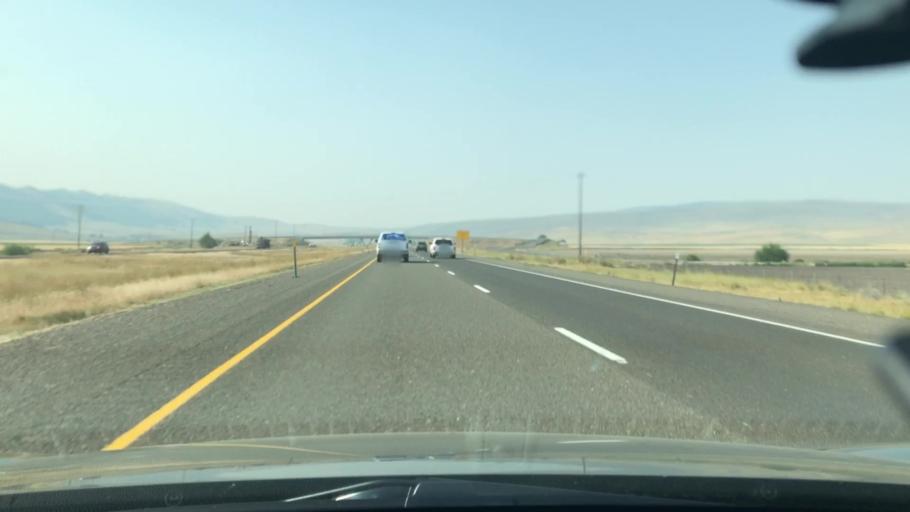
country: US
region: Oregon
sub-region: Union County
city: Union
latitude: 45.0922
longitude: -117.9516
